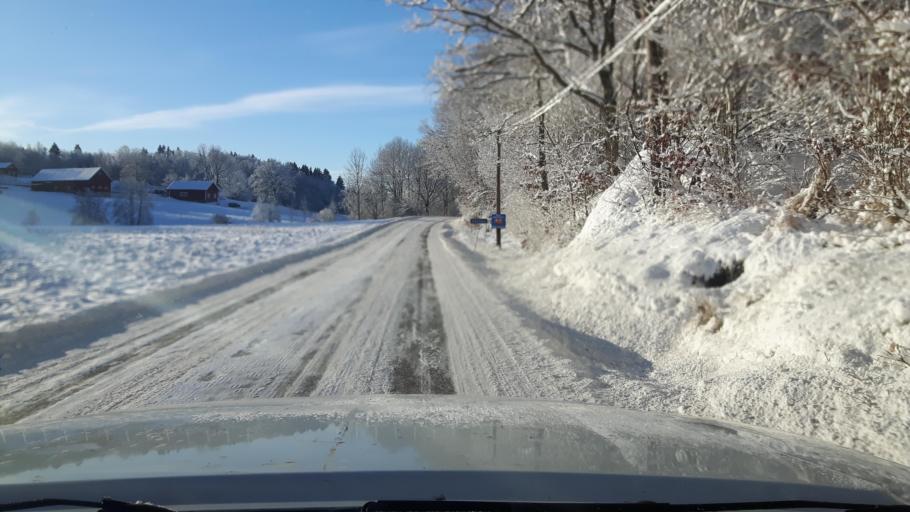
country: SE
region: Halland
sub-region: Kungsbacka Kommun
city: Fjaeras kyrkby
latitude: 57.5672
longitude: 12.2191
